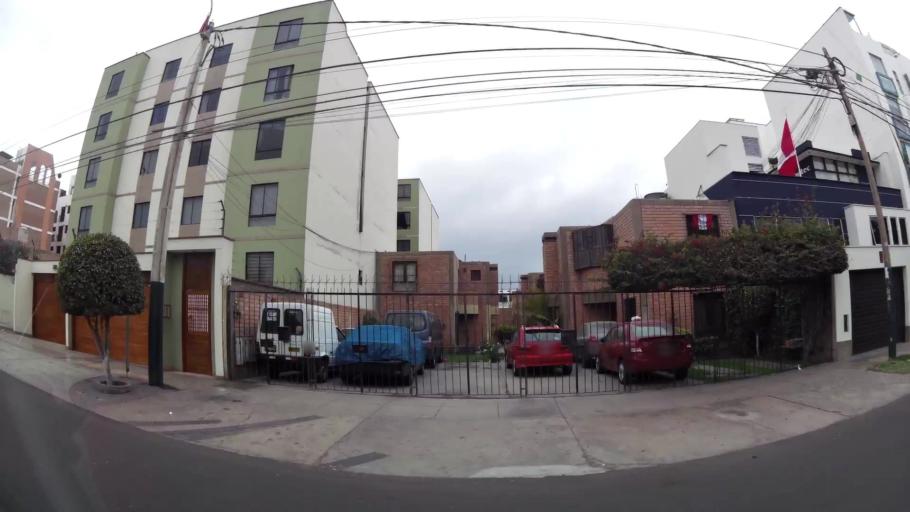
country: PE
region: Lima
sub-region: Lima
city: Surco
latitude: -12.1431
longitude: -76.9964
